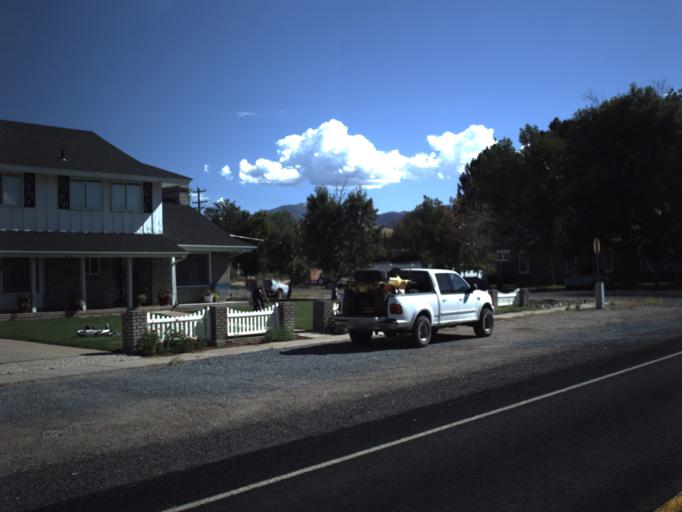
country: US
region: Utah
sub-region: Beaver County
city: Beaver
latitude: 38.2770
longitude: -112.6298
